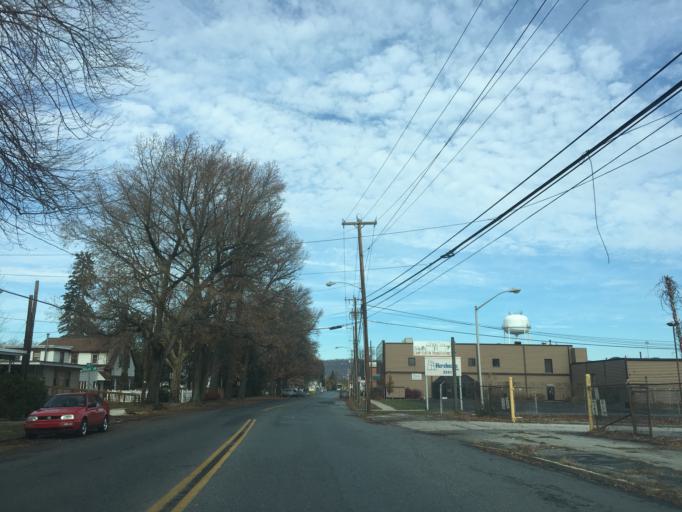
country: US
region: Pennsylvania
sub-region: Dauphin County
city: Harrisburg
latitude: 40.3023
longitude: -76.8959
